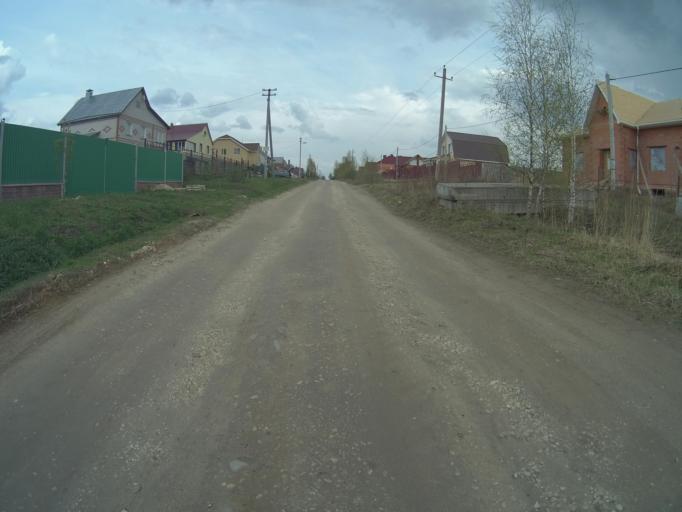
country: RU
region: Vladimir
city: Kommunar
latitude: 56.0581
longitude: 40.4863
